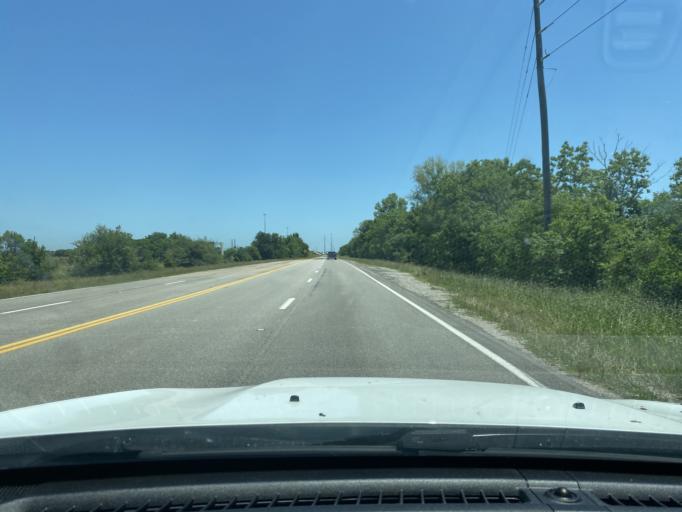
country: US
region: Texas
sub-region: Waller County
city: Waller
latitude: 30.0254
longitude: -95.8407
